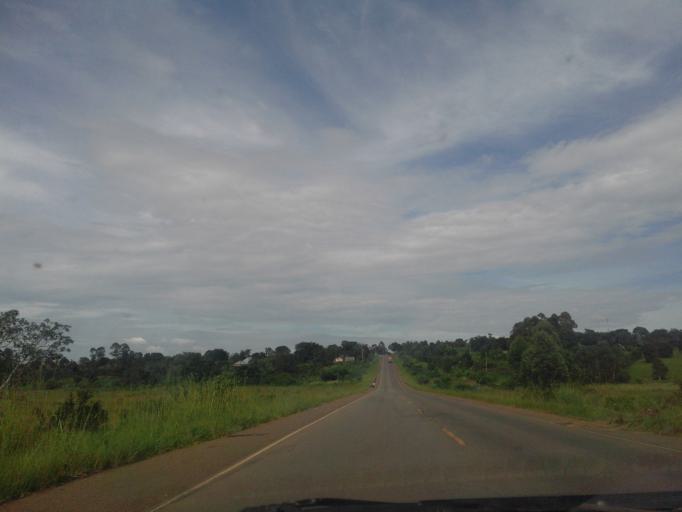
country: UG
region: Central Region
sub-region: Lwengo District
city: Lwengo
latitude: -0.3618
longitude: 31.5424
